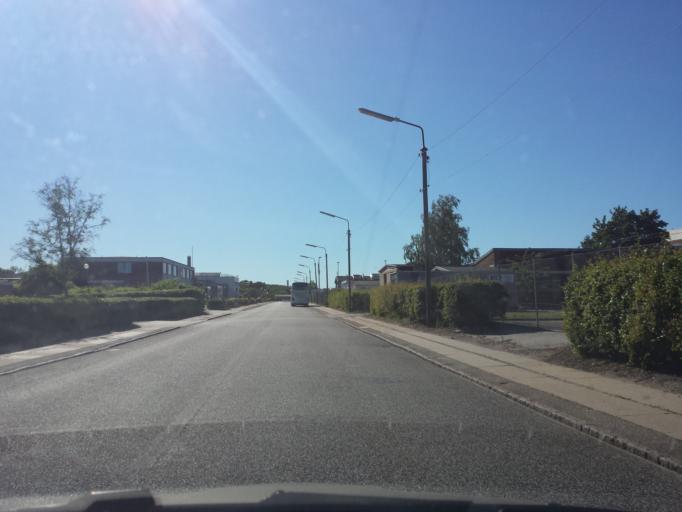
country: DK
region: Capital Region
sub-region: Ballerup Kommune
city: Ballerup
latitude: 55.7252
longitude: 12.3930
